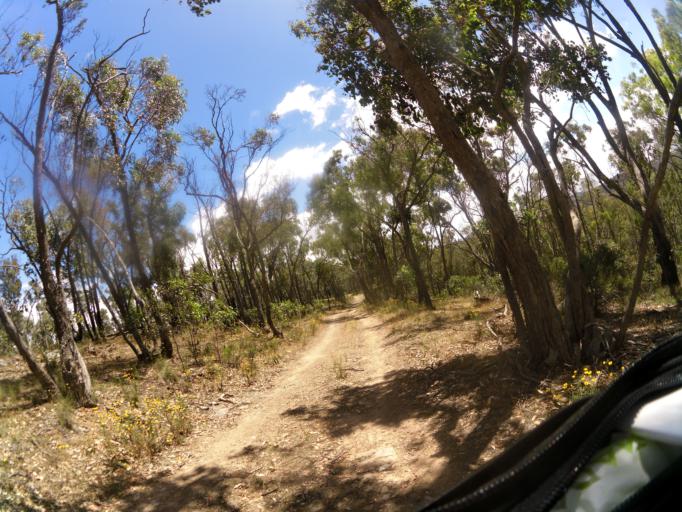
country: AU
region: Victoria
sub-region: Mount Alexander
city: Castlemaine
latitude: -37.0678
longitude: 144.2652
